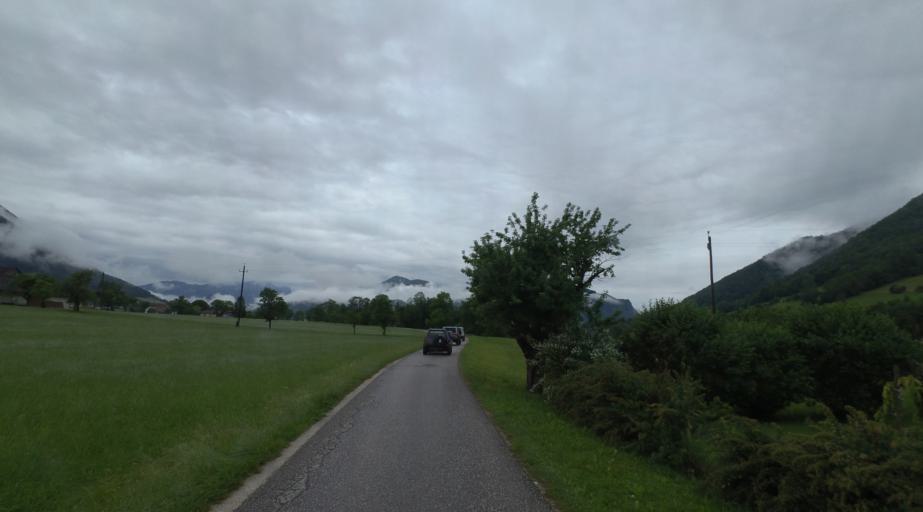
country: AT
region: Upper Austria
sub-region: Politischer Bezirk Kirchdorf an der Krems
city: Gruenburg
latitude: 47.8931
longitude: 14.2764
